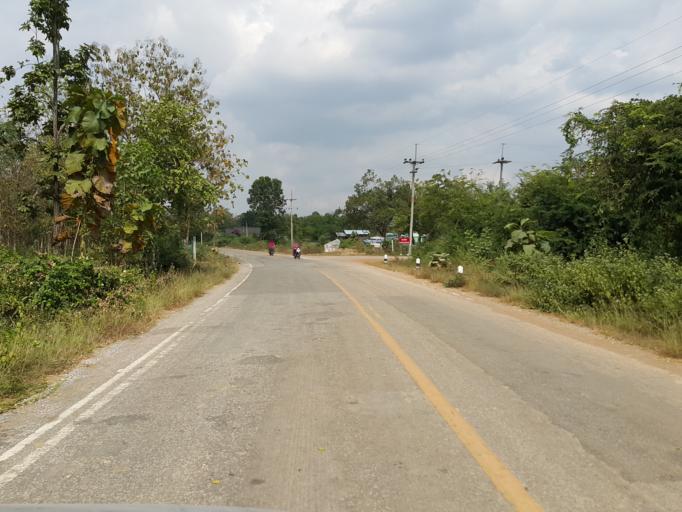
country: TH
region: Sukhothai
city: Thung Saliam
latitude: 17.3677
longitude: 99.5953
